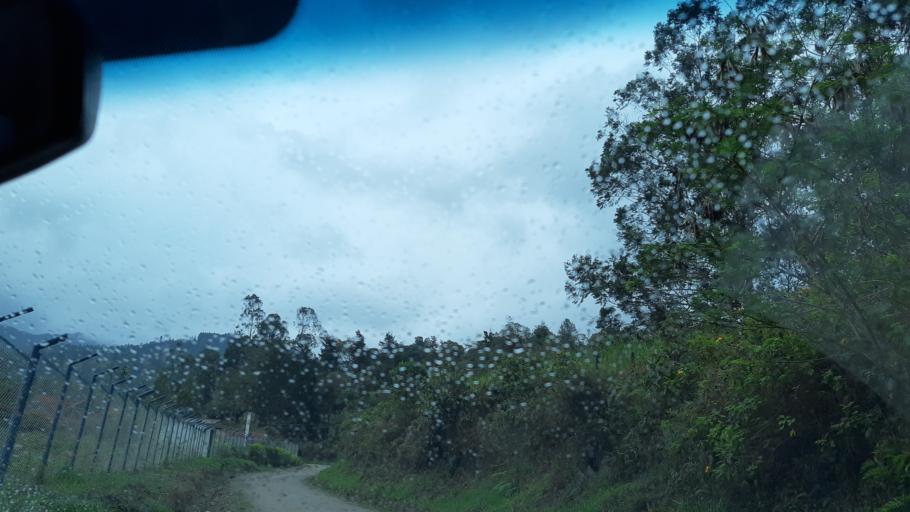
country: CO
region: Boyaca
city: Chivor
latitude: 4.9623
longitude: -73.3164
